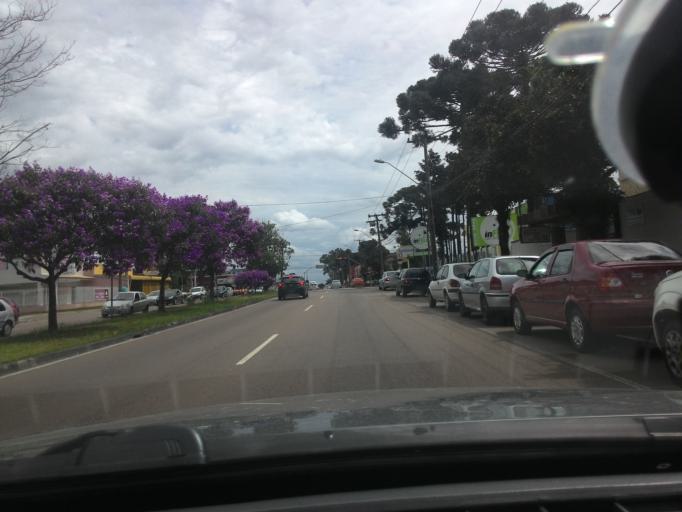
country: BR
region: Parana
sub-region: Pinhais
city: Pinhais
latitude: -25.4582
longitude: -49.2326
